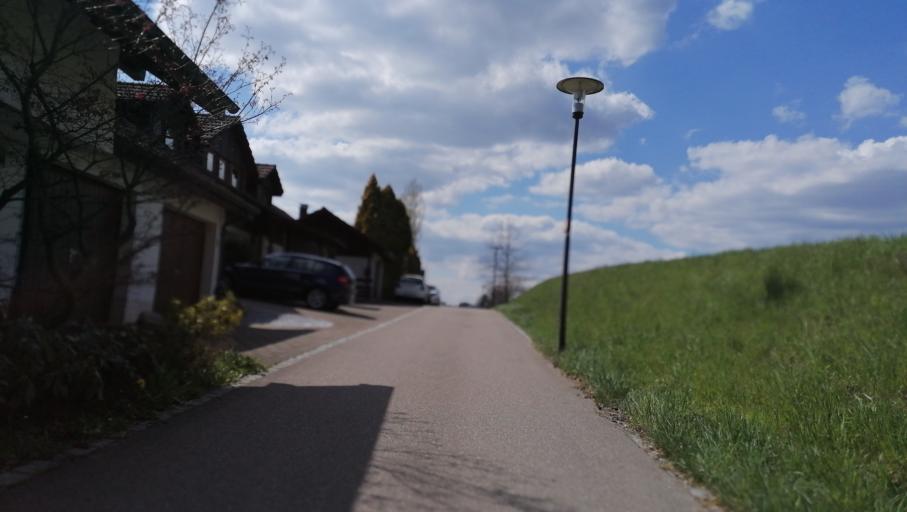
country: CH
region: Aargau
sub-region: Bezirk Rheinfelden
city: Stein
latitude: 47.5624
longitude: 7.9727
